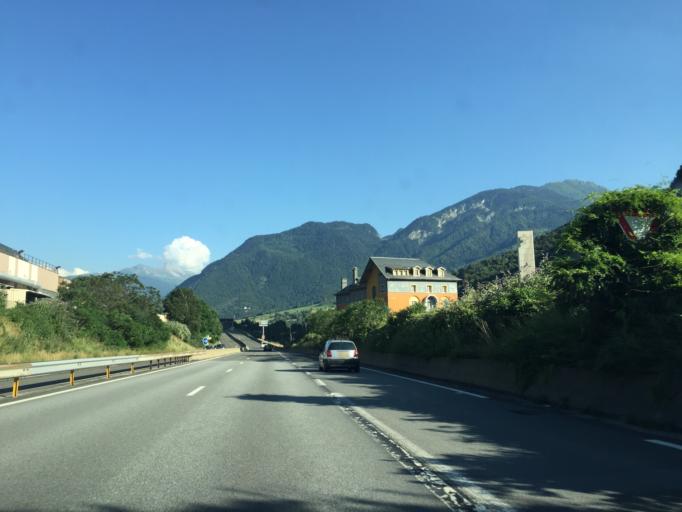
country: FR
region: Rhone-Alpes
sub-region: Departement de la Savoie
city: Aigueblanche
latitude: 45.5243
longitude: 6.4825
